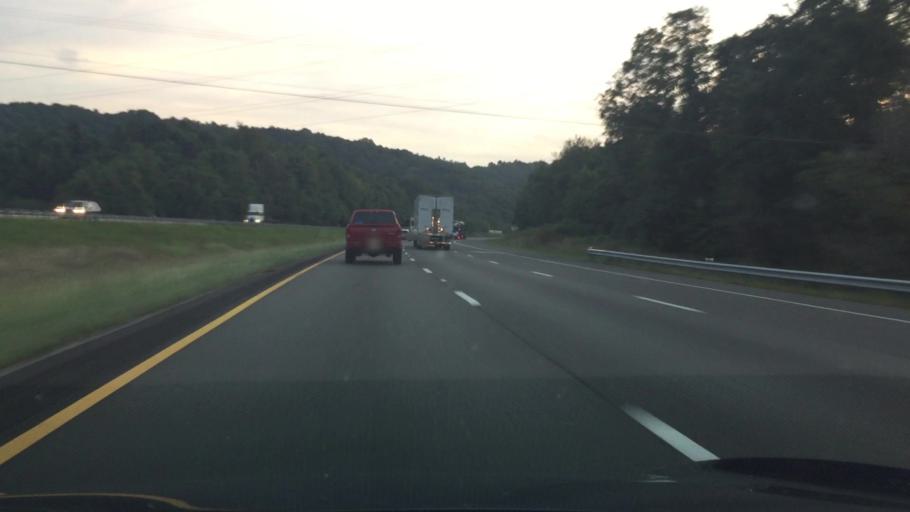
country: US
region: Virginia
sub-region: Montgomery County
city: Shawsville
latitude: 37.2528
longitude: -80.1814
